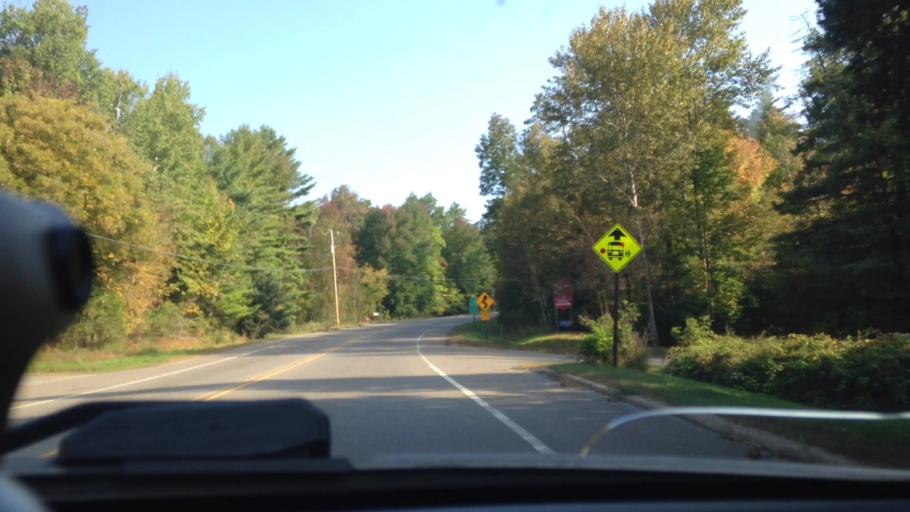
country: US
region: Michigan
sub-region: Dickinson County
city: Quinnesec
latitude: 45.8083
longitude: -87.9884
